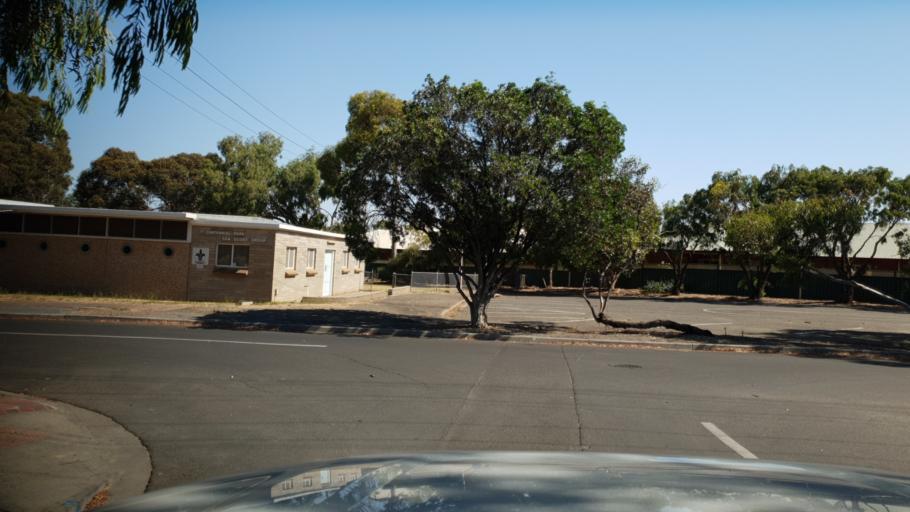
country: AU
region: South Australia
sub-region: Marion
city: Clovelly Park
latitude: -34.9963
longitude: 138.5835
